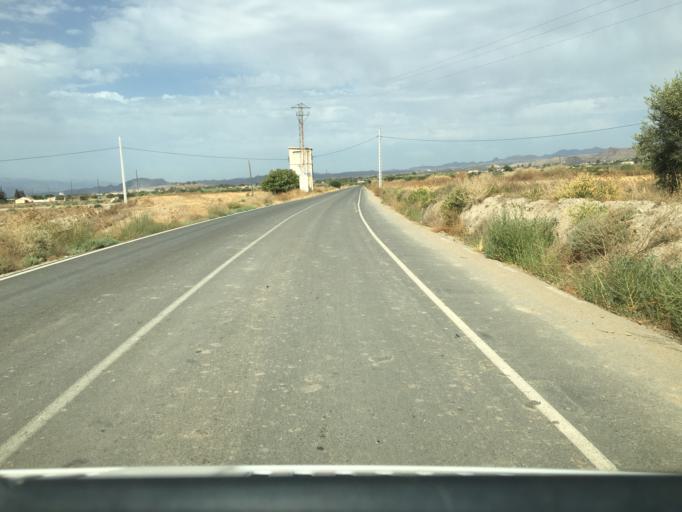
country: ES
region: Andalusia
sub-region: Provincia de Almeria
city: Huercal-Overa
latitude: 37.4210
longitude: -1.8966
